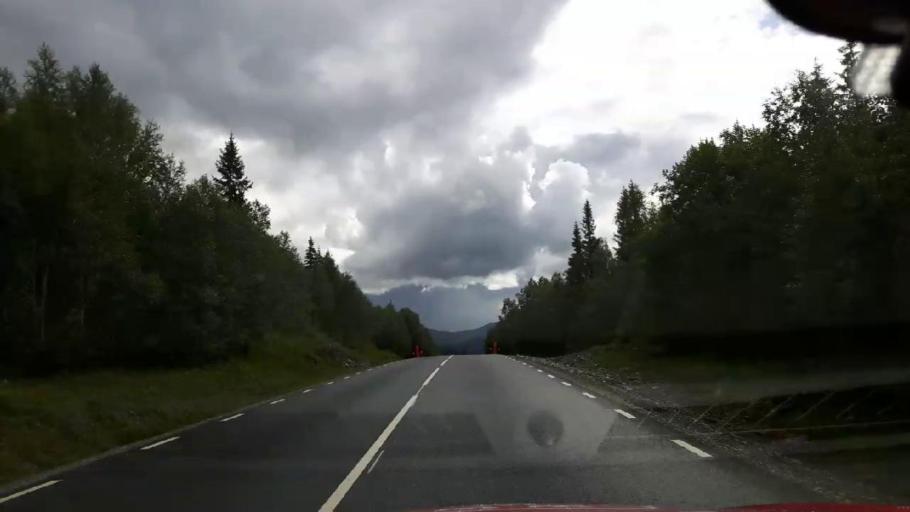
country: NO
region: Nord-Trondelag
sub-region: Royrvik
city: Royrvik
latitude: 64.8831
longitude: 14.2061
